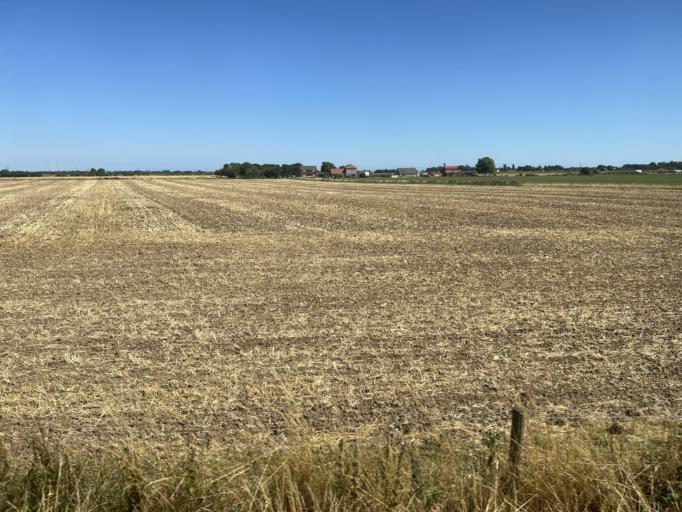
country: GB
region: England
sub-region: Lincolnshire
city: Wainfleet All Saints
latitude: 53.1100
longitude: 0.2241
